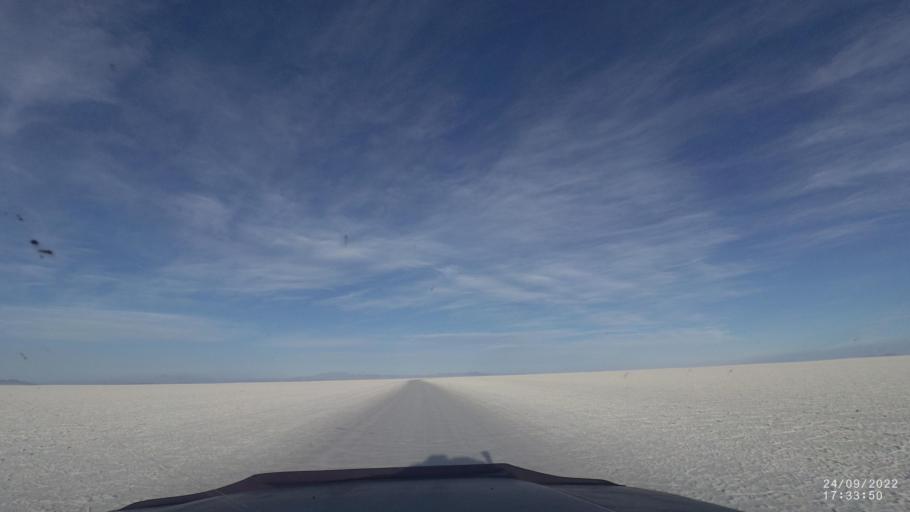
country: BO
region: Potosi
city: Colchani
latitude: -20.3201
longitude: -67.2963
